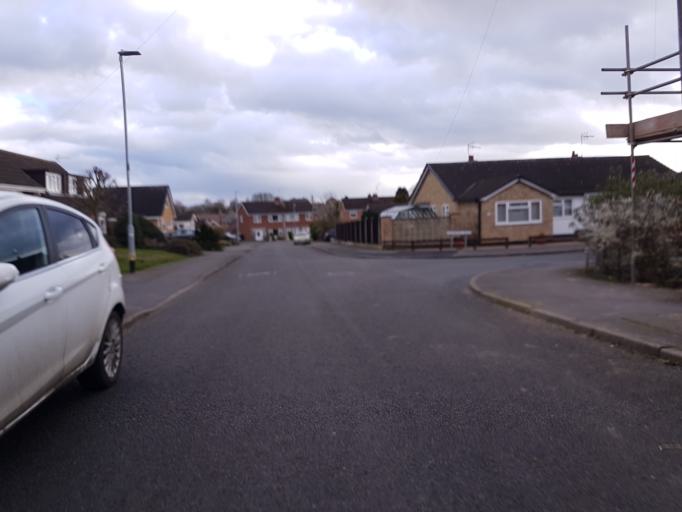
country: GB
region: England
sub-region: Leicestershire
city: Earl Shilton
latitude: 52.5684
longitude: -1.3204
